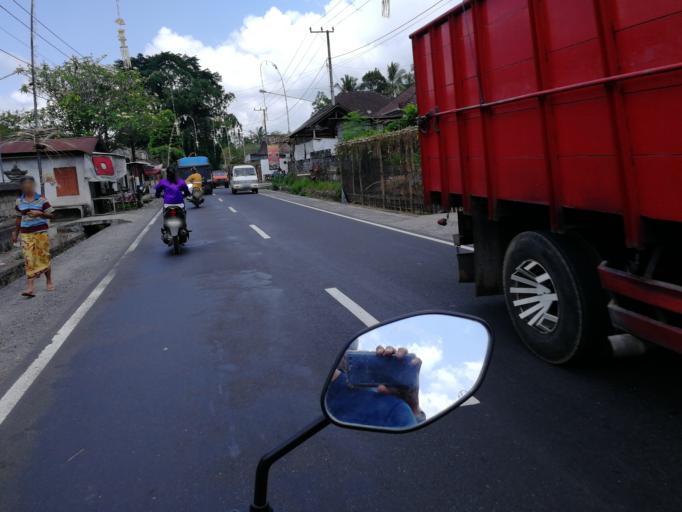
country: ID
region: Bali
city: Banjar Kubu
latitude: -8.4286
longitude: 115.4199
